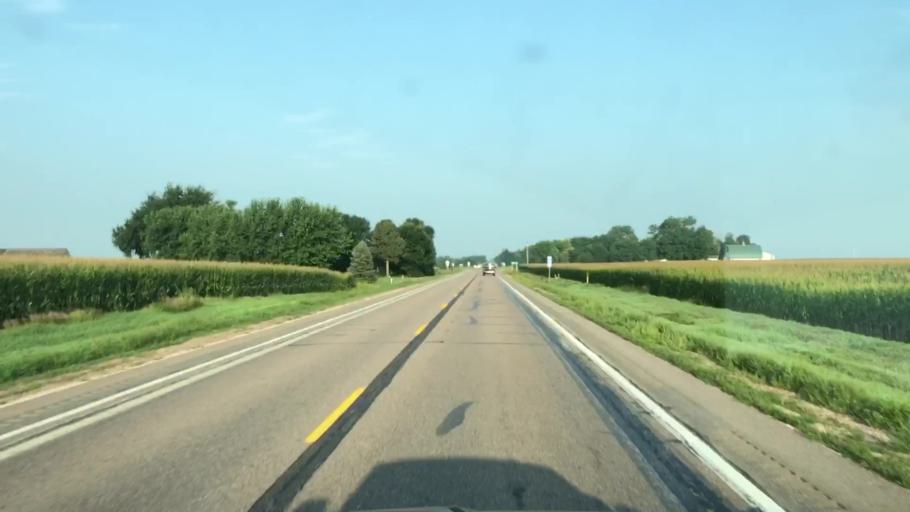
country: US
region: Iowa
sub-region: O'Brien County
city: Sheldon
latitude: 43.1860
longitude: -95.9174
